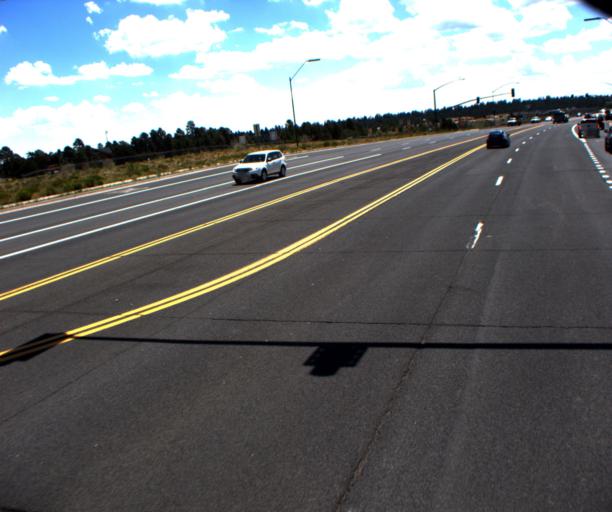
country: US
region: Arizona
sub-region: Coconino County
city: Flagstaff
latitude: 35.2190
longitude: -111.5851
